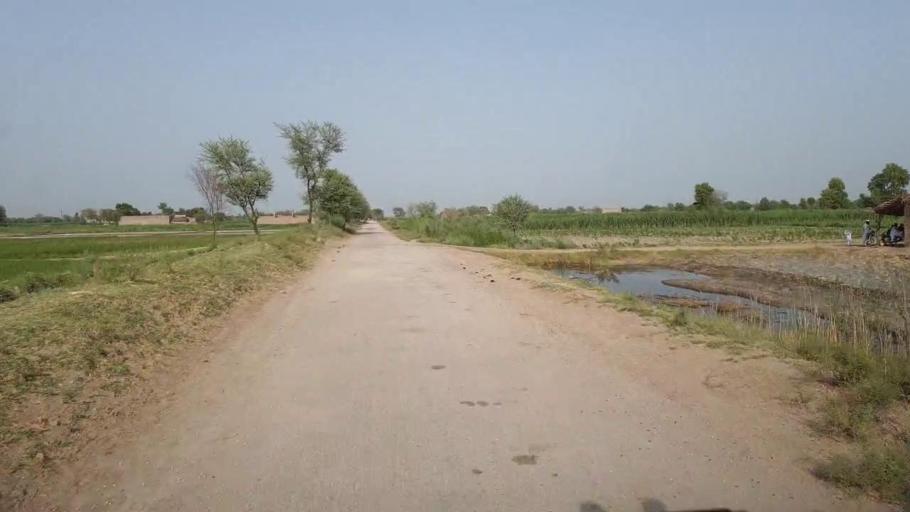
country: PK
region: Sindh
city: Daur
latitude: 26.3409
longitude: 68.1846
